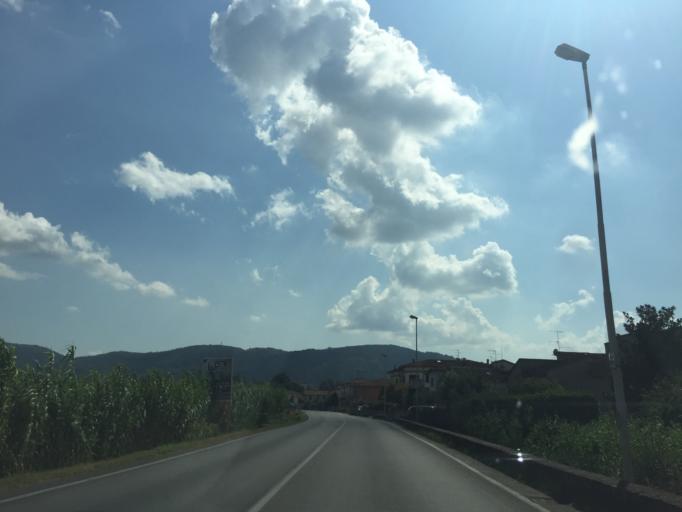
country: IT
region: Tuscany
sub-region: Provincia di Pistoia
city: Cantagrillo-Casalguidi
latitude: 43.8826
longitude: 10.9163
